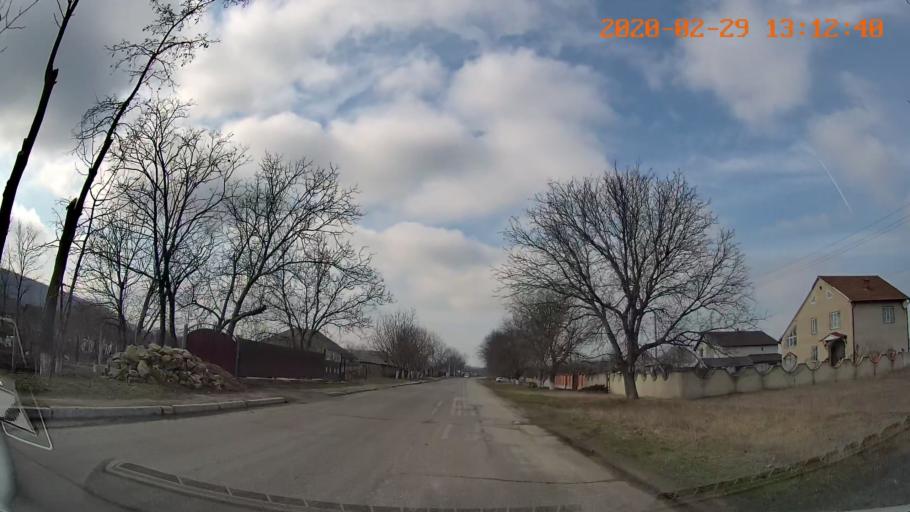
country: MD
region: Telenesti
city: Camenca
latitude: 48.0132
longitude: 28.6931
